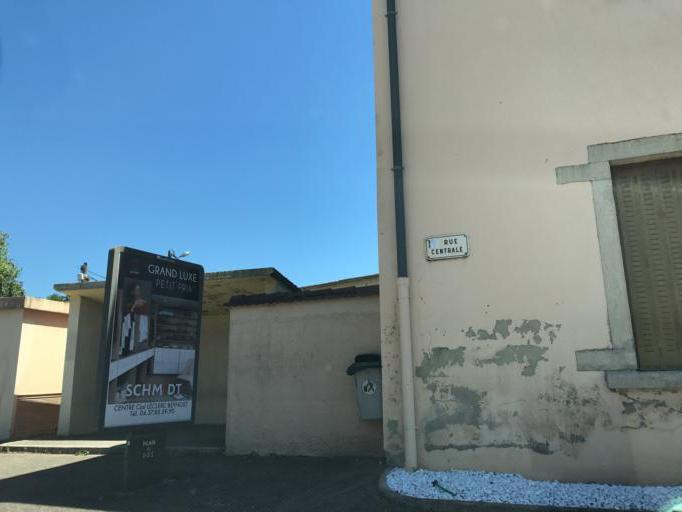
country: FR
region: Rhone-Alpes
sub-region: Departement de l'Ain
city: Balan
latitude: 45.8350
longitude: 5.1009
